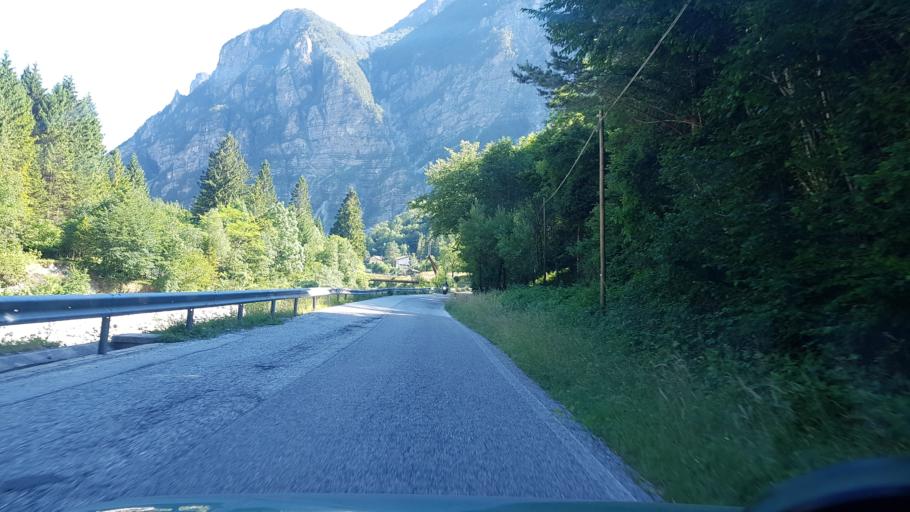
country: IT
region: Friuli Venezia Giulia
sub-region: Provincia di Udine
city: Moggio Udinese
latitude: 46.4538
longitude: 13.1880
